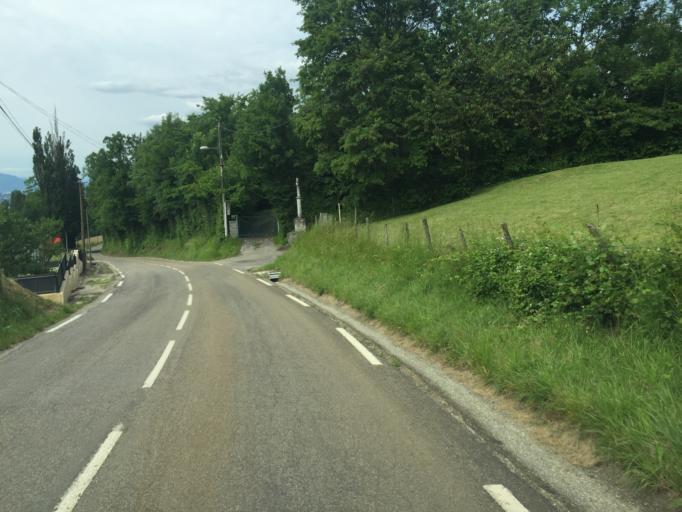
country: FR
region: Rhone-Alpes
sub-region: Departement de la Savoie
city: Jacob-Bellecombette
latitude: 45.5342
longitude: 5.9156
